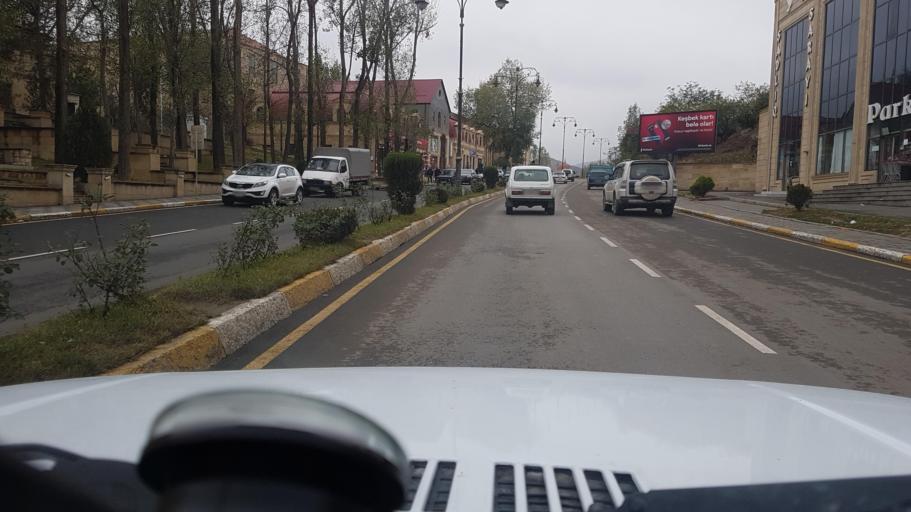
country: AZ
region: Gadabay Rayon
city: Kyadabek
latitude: 40.5775
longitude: 45.8087
